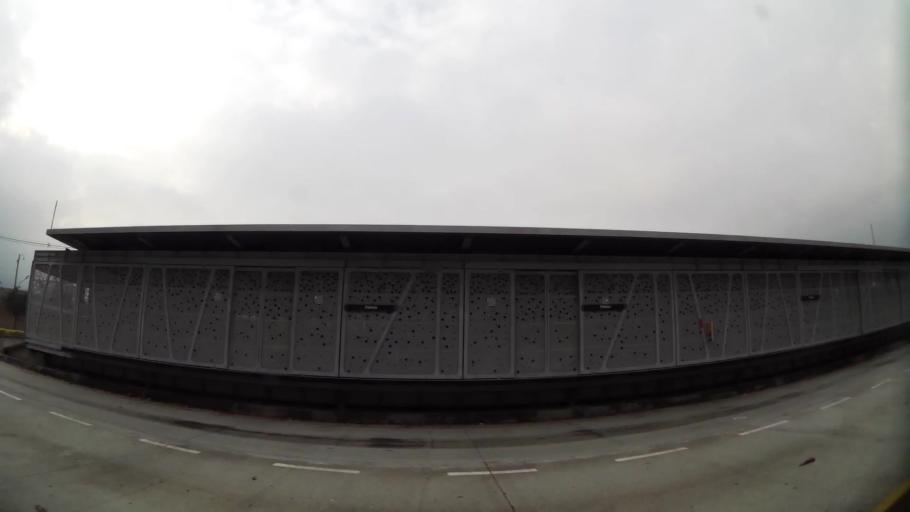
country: CO
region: Antioquia
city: Medellin
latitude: 6.2318
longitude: -75.5867
